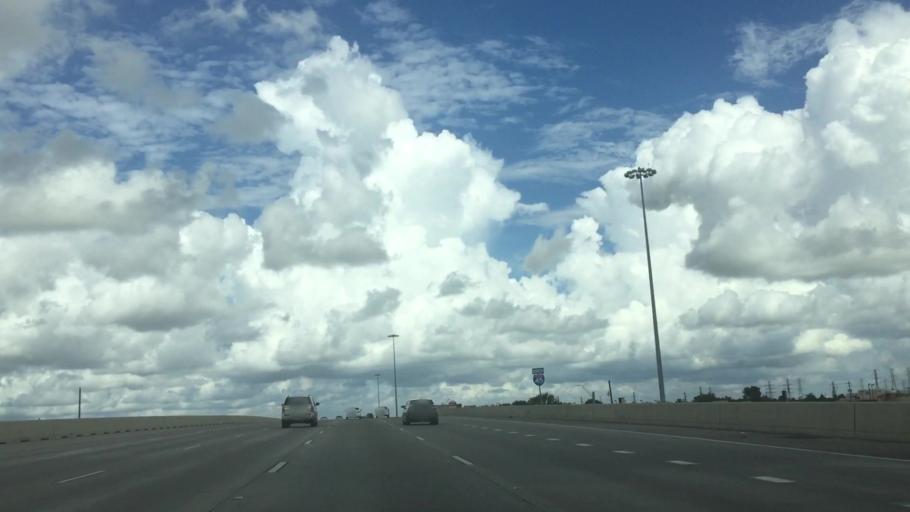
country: US
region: Texas
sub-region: Harris County
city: Webster
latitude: 29.5525
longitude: -95.1527
